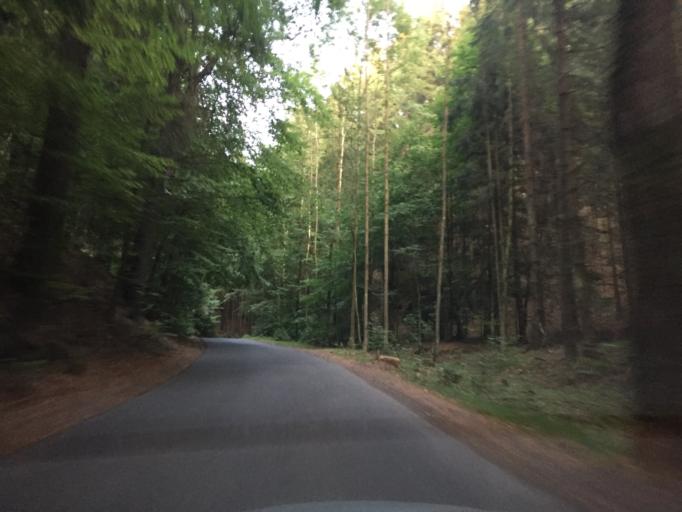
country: CZ
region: Ustecky
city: Ceska Kamenice
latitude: 50.8500
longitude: 14.4122
